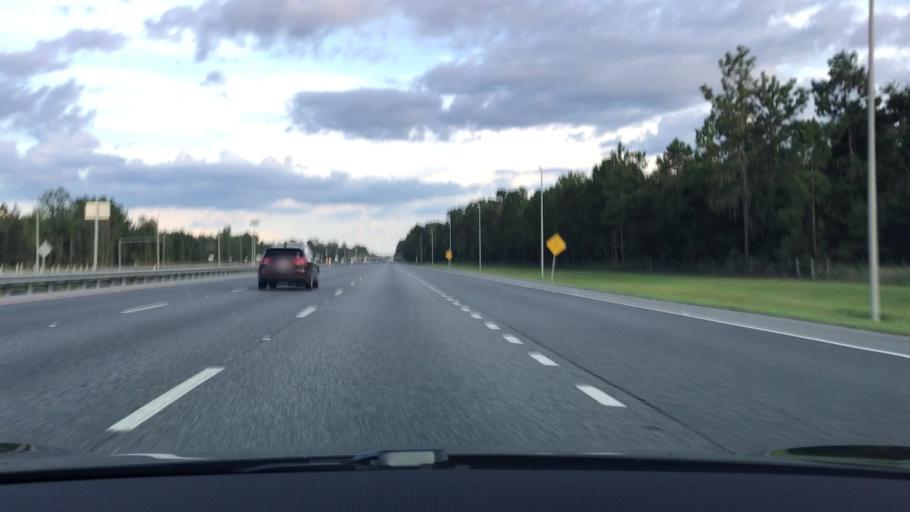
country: US
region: Florida
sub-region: Hamilton County
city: Jasper
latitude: 30.4145
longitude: -82.8973
